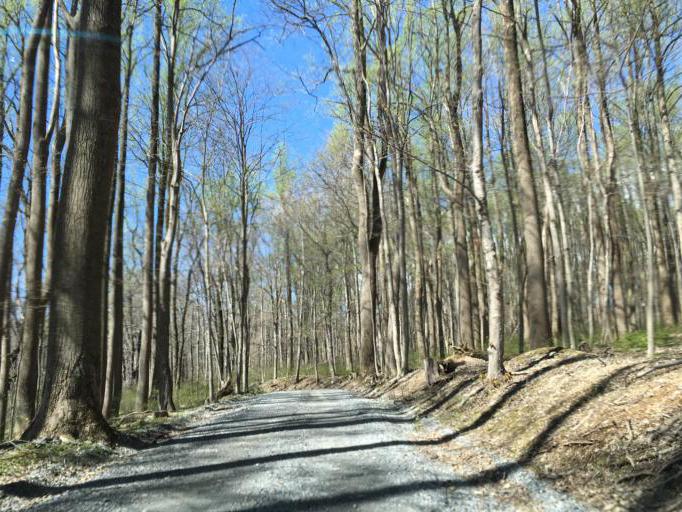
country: US
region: Maryland
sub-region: Washington County
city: Highfield-Cascade
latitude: 39.6564
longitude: -77.4776
